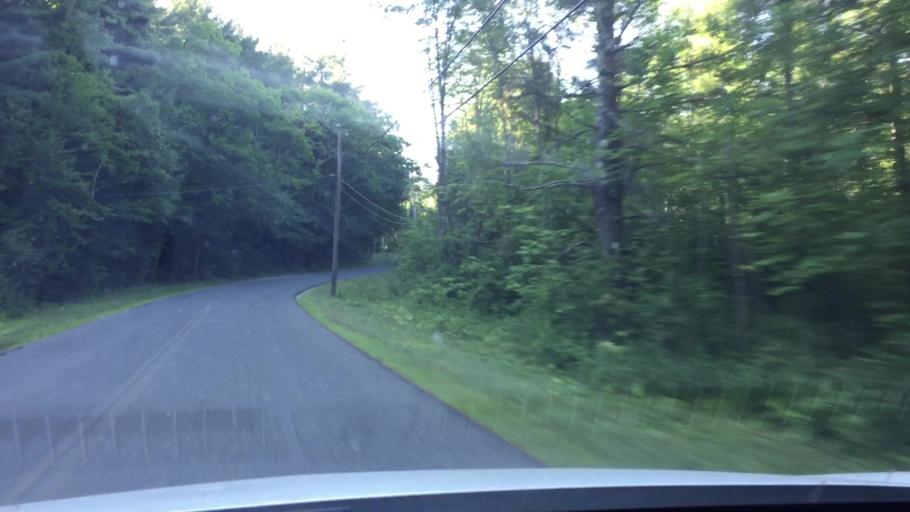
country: US
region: Massachusetts
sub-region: Berkshire County
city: Lee
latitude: 42.2786
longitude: -73.2088
